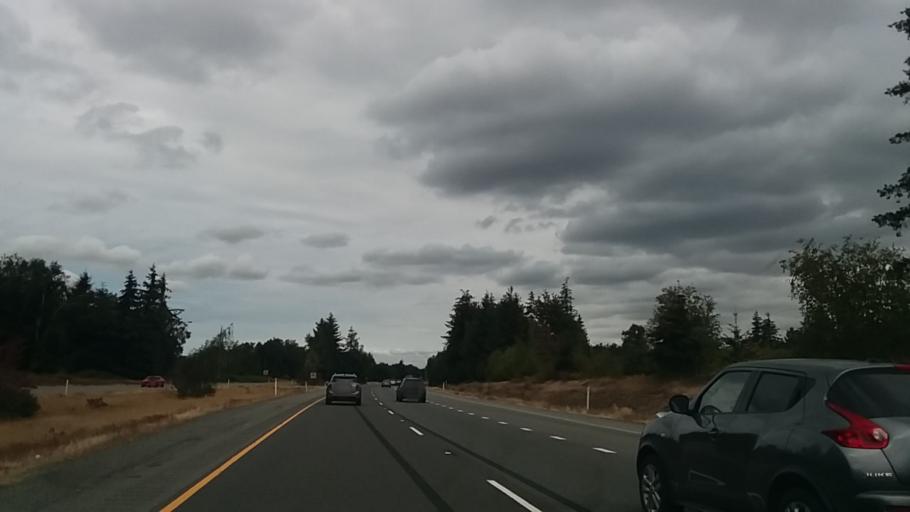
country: US
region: Washington
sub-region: Whatcom County
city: Ferndale
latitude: 48.9114
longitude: -122.6265
